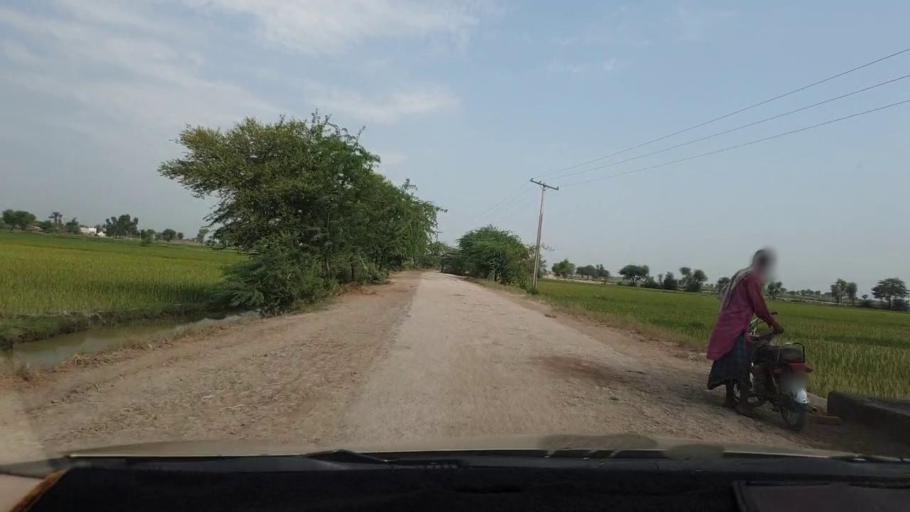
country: PK
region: Sindh
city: Larkana
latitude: 27.6734
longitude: 68.2206
